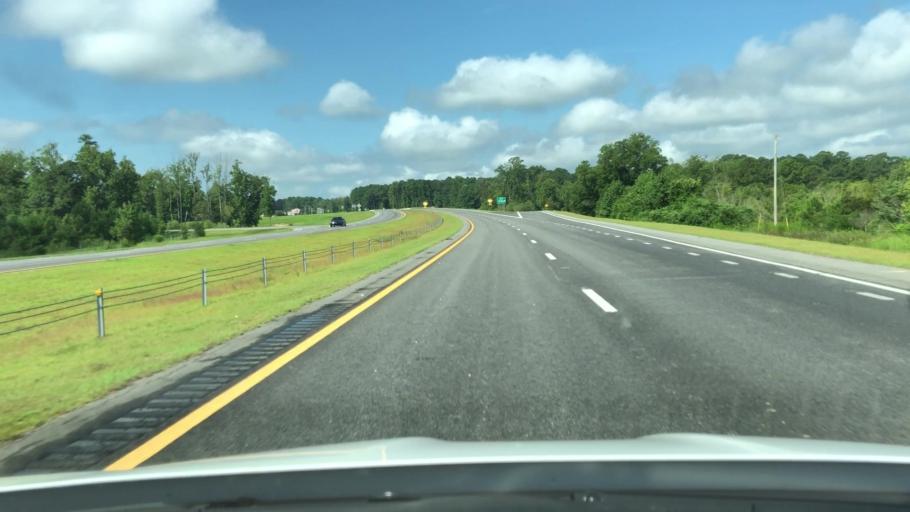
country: US
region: North Carolina
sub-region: Bertie County
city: Windsor
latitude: 36.0131
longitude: -76.9490
